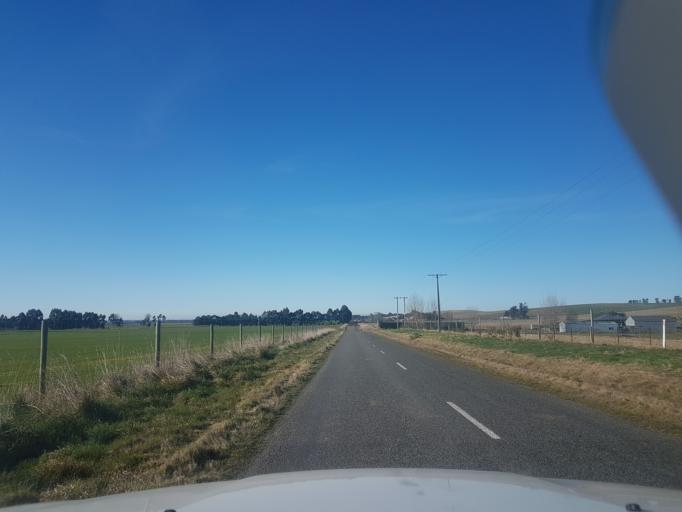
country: NZ
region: Canterbury
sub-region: Timaru District
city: Pleasant Point
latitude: -44.2920
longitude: 171.0572
